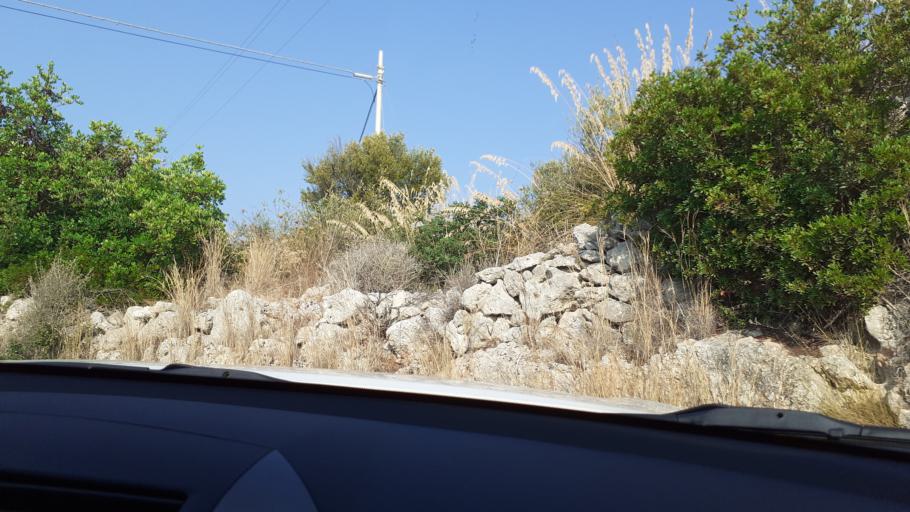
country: IT
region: Sicily
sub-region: Provincia di Siracusa
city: Cassibile
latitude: 36.9805
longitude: 15.1705
